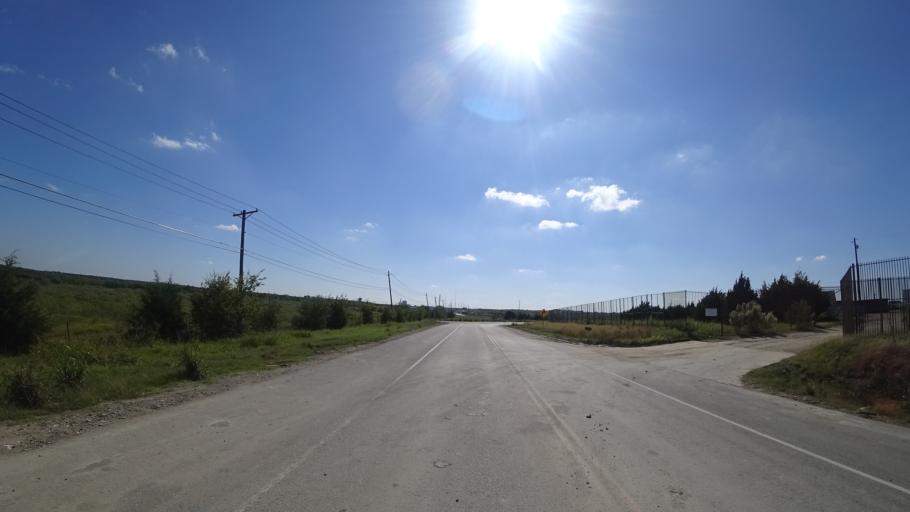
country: US
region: Texas
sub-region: Travis County
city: Manor
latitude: 30.3319
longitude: -97.6024
